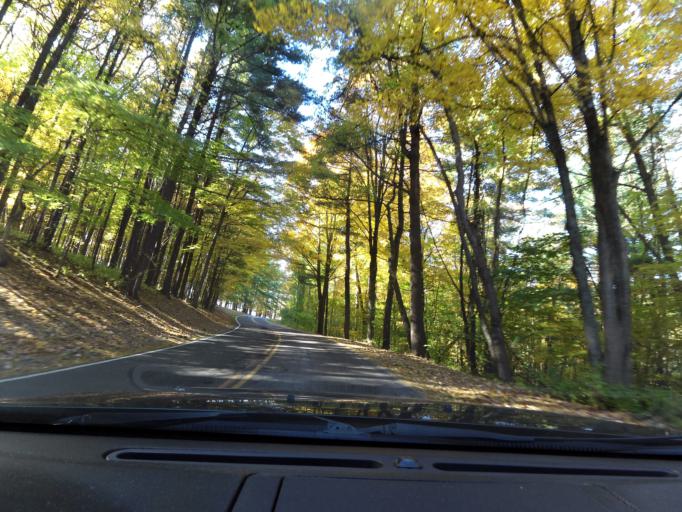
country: US
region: New York
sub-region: Wyoming County
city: Castile
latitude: 42.6084
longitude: -78.0220
